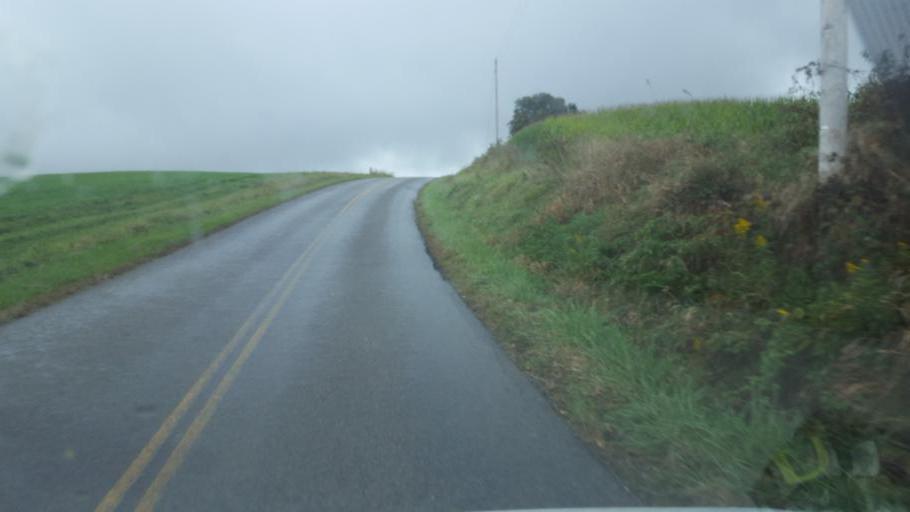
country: US
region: Ohio
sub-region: Holmes County
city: Millersburg
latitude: 40.5512
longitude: -82.0029
